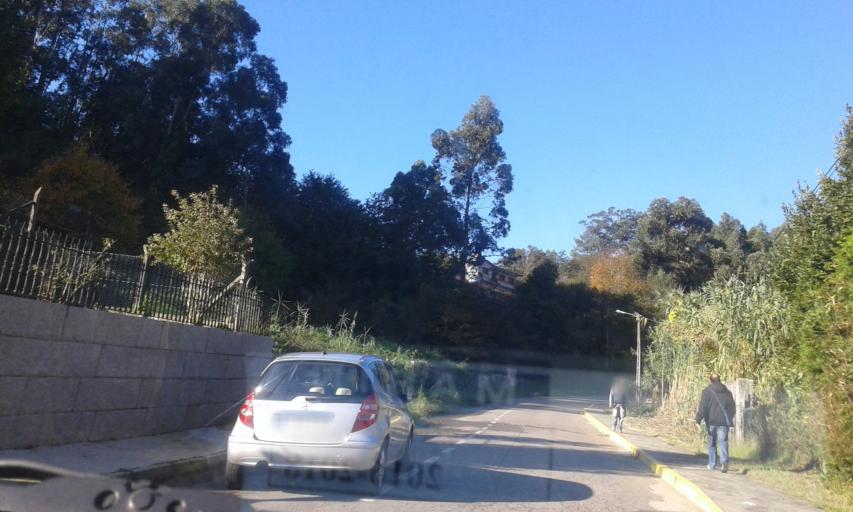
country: ES
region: Galicia
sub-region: Provincia de Pontevedra
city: Marin
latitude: 42.3832
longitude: -8.7200
